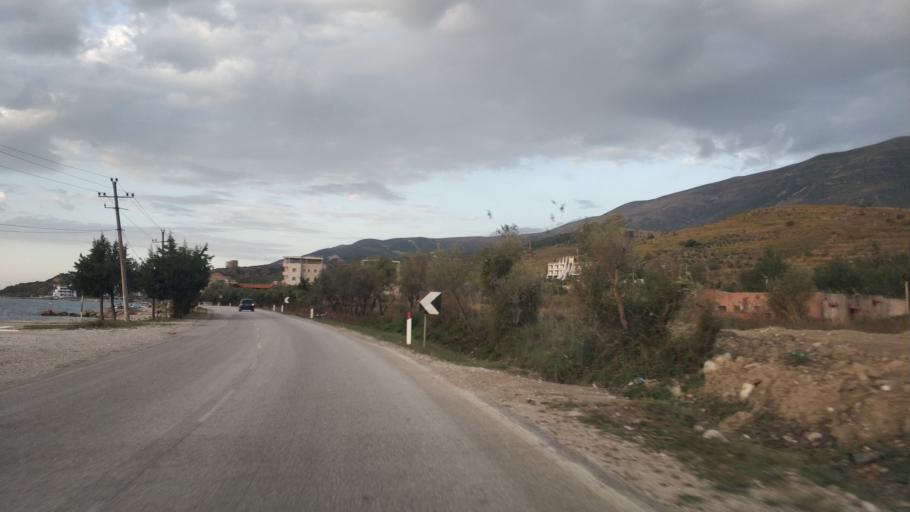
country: AL
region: Vlore
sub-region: Rrethi i Vlores
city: Orikum
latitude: 40.3475
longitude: 19.4856
